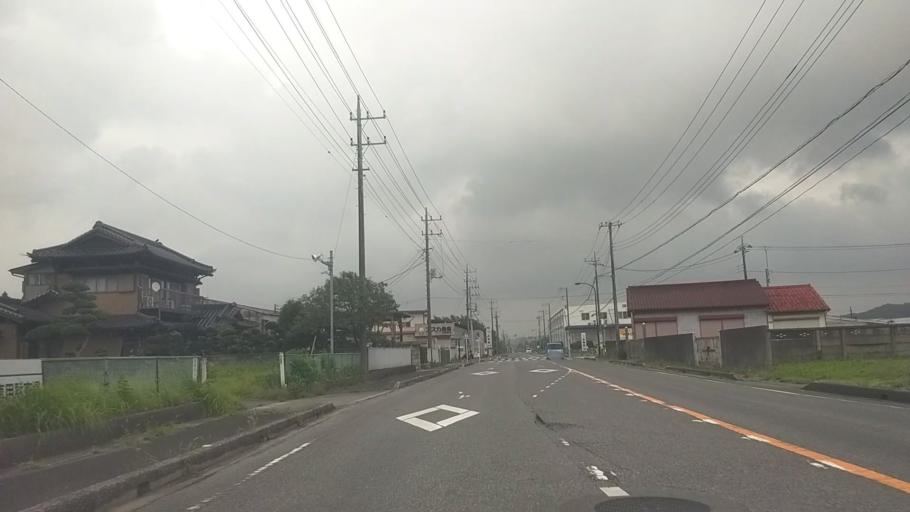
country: JP
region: Chiba
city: Ohara
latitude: 35.2866
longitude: 140.2625
